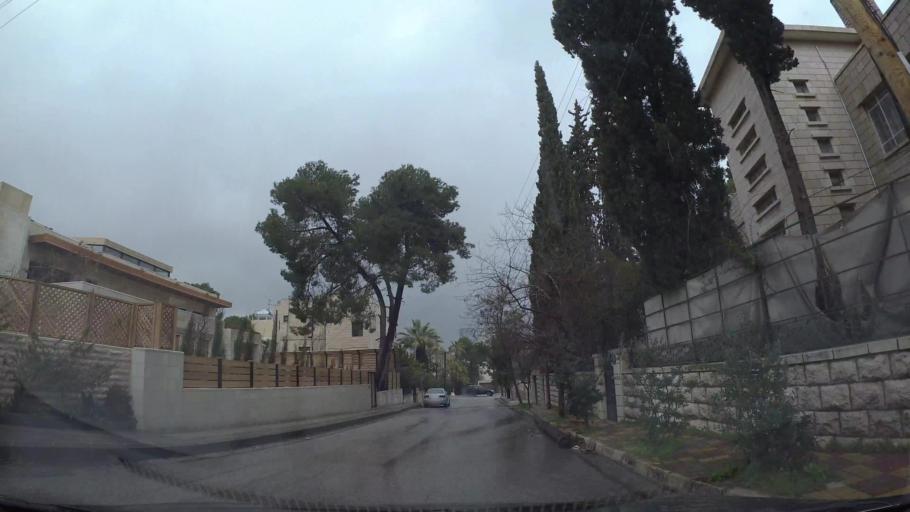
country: JO
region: Amman
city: Amman
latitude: 31.9563
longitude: 35.9046
